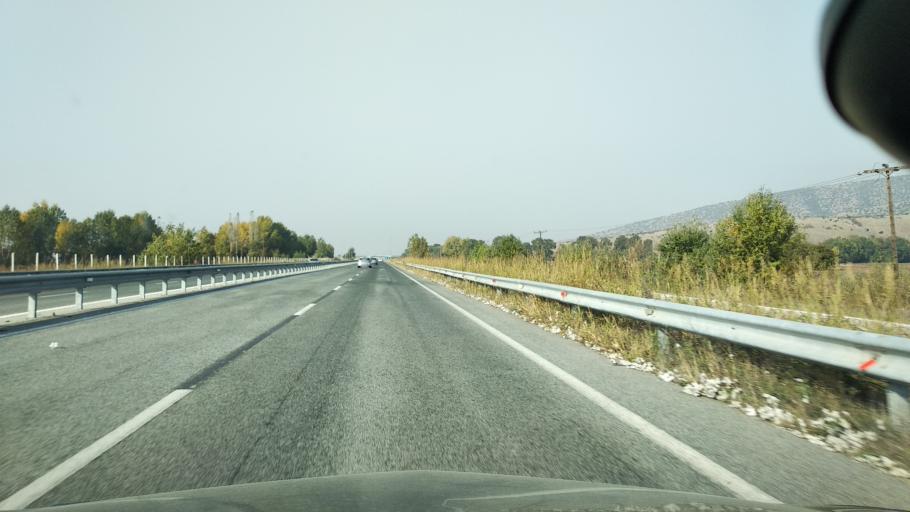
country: GR
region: Thessaly
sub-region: Trikala
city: Oichalia
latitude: 39.5647
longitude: 21.9501
